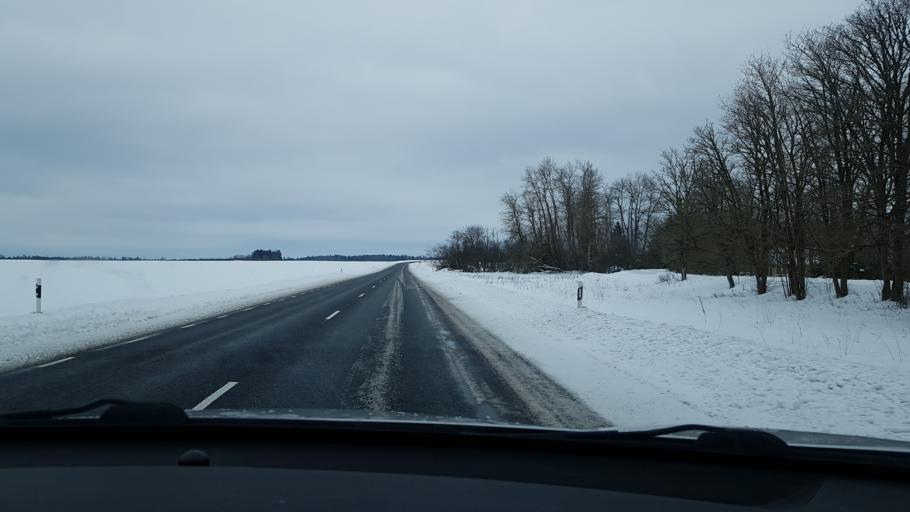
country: EE
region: Jaervamaa
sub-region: Jaerva-Jaani vald
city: Jarva-Jaani
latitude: 59.1202
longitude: 25.7894
